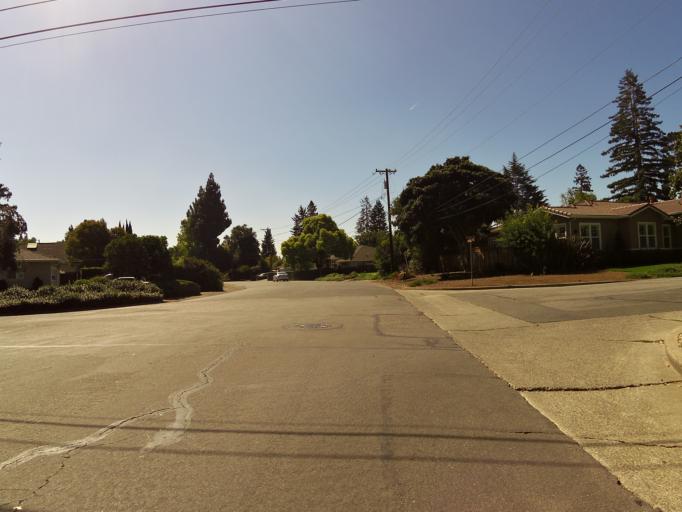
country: US
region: California
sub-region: Santa Clara County
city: Los Altos
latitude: 37.3939
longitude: -122.1038
